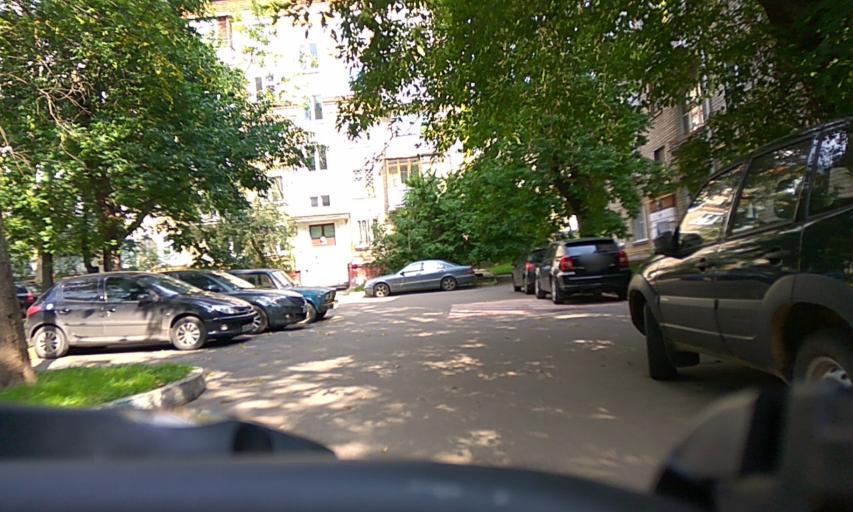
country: RU
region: Moscow
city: Tsaritsyno
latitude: 55.6469
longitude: 37.6629
